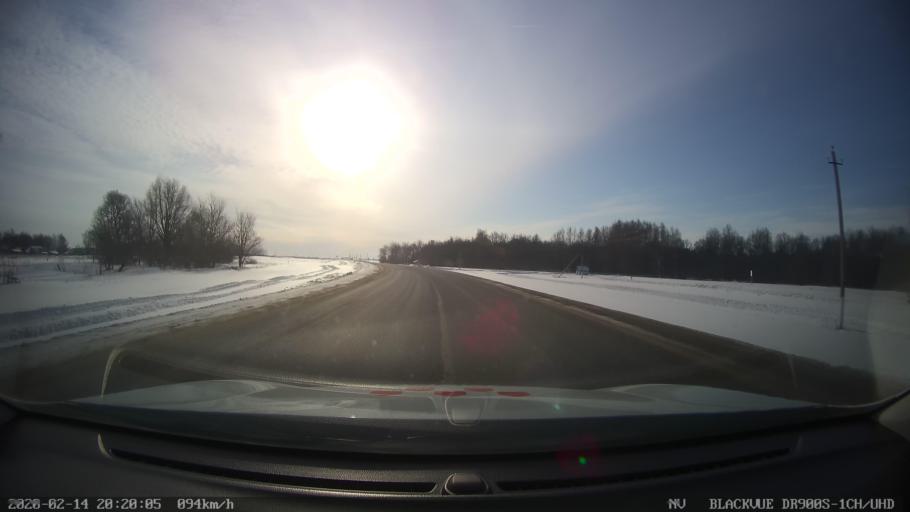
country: RU
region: Tatarstan
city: Verkhniy Uslon
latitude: 55.5611
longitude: 48.9018
